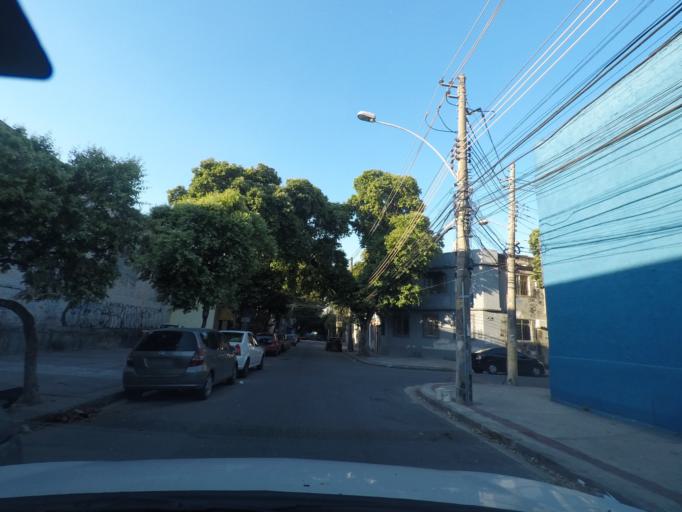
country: BR
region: Rio de Janeiro
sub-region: Rio De Janeiro
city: Rio de Janeiro
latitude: -22.9133
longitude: -43.2008
